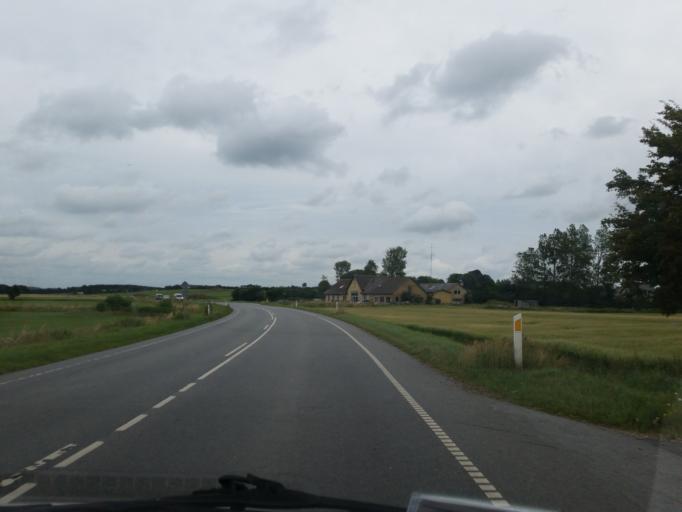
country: DK
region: South Denmark
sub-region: Vejen Kommune
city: Holsted
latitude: 55.4033
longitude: 8.9319
